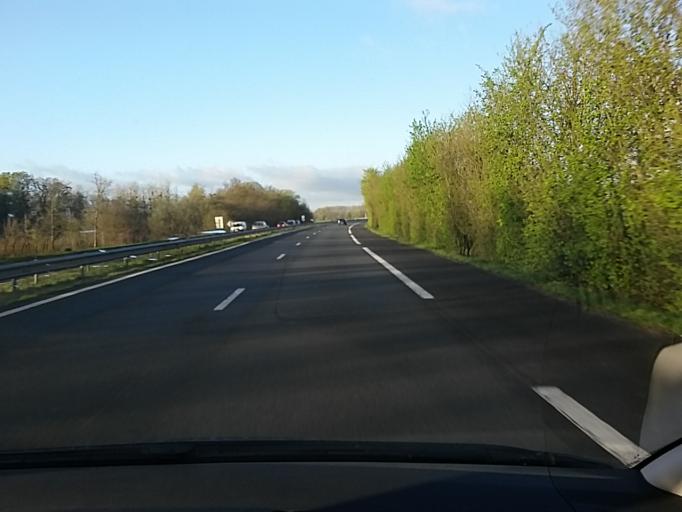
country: FR
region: Picardie
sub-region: Departement de l'Oise
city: Lacroix-Saint-Ouen
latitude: 49.3676
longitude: 2.7763
